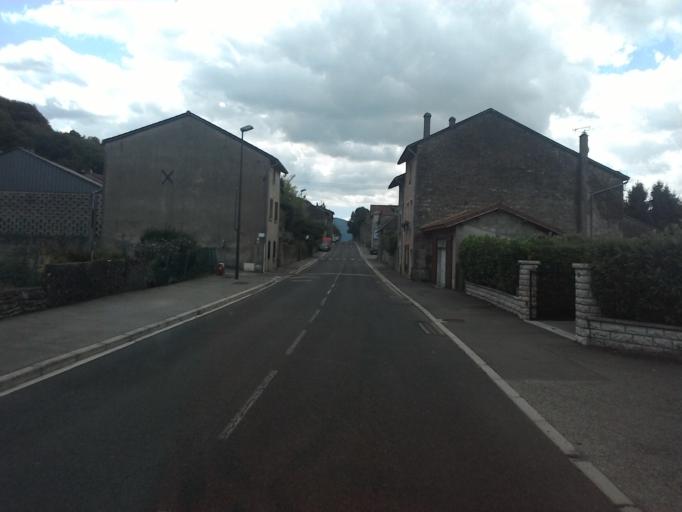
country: FR
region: Rhone-Alpes
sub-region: Departement de l'Ain
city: Sault-Brenaz
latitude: 45.8647
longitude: 5.3951
